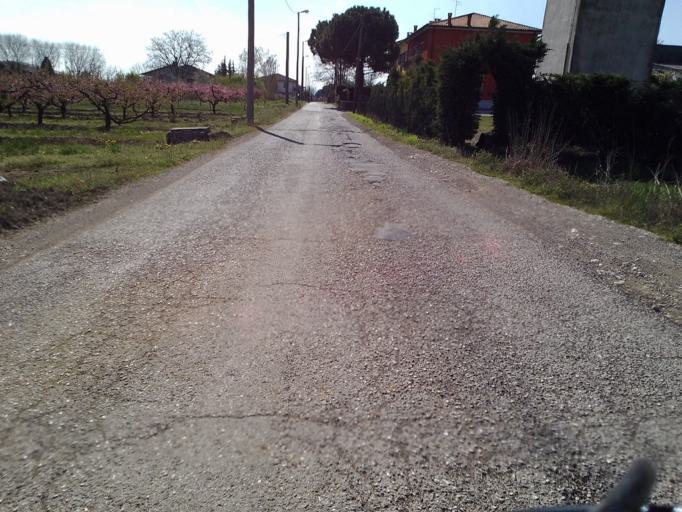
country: IT
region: Veneto
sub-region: Provincia di Verona
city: Dossobuono
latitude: 45.3993
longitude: 10.9322
